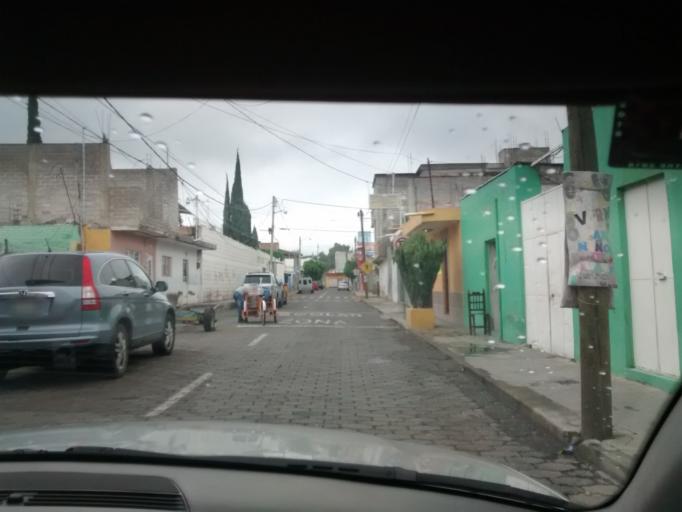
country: MX
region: Puebla
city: Tehuacan
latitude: 18.4551
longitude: -97.3951
